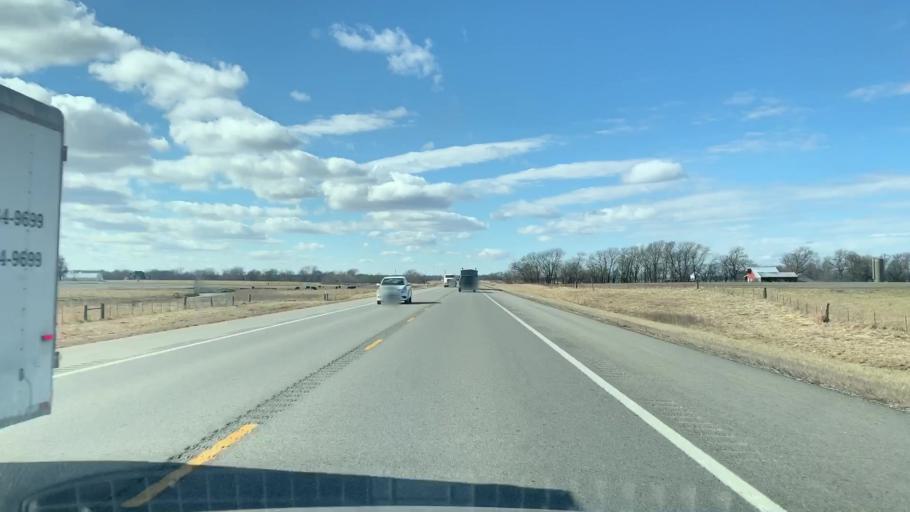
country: US
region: Kansas
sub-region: Crawford County
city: Pittsburg
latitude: 37.3396
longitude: -94.8536
